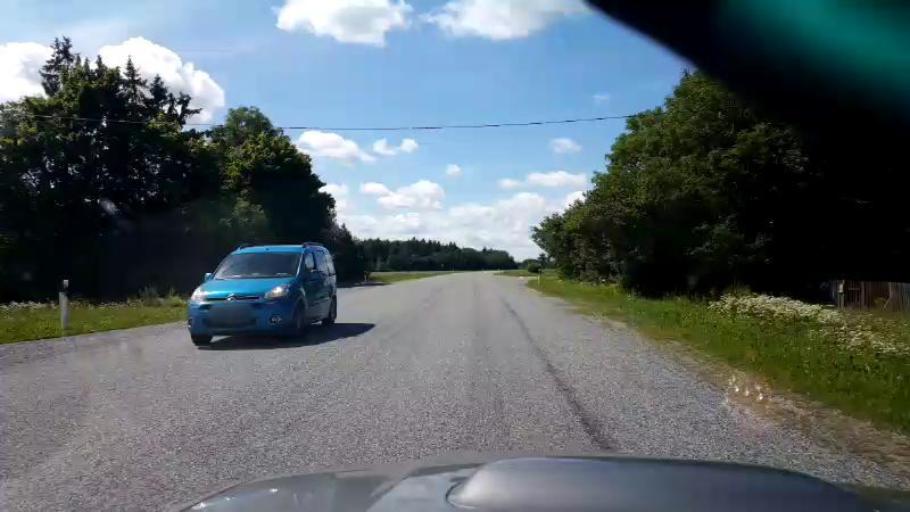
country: EE
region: Laeaene-Virumaa
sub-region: Tapa vald
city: Tapa
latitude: 59.2145
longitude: 25.8799
